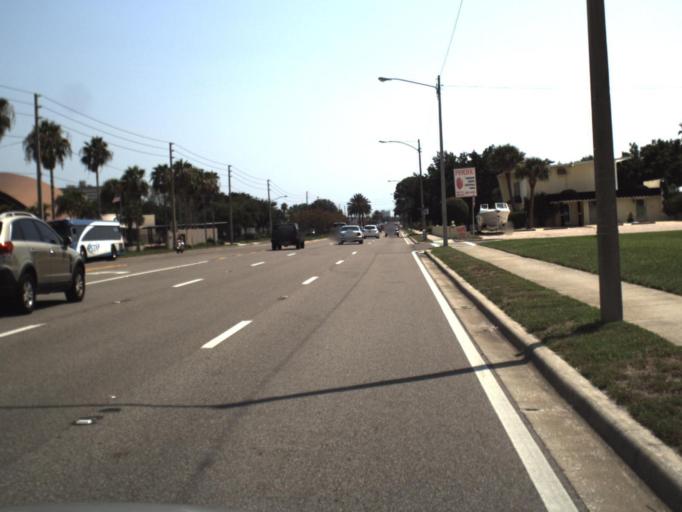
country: US
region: Florida
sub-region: Pinellas County
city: South Pasadena
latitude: 27.7681
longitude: -82.7331
